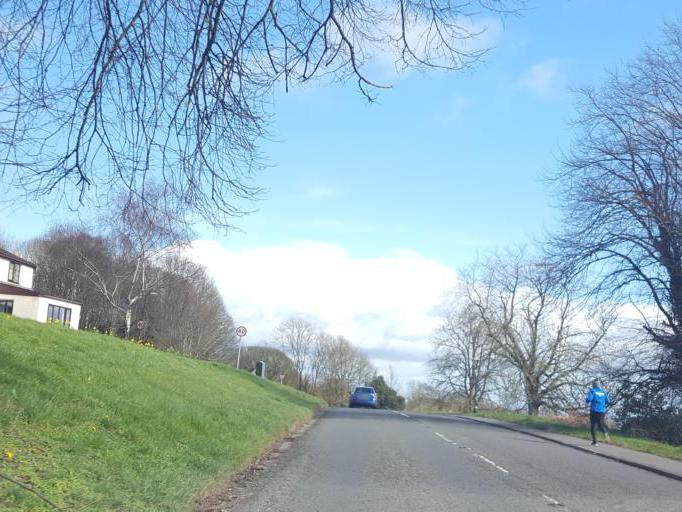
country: GB
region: England
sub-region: Worcestershire
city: Great Malvern
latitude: 52.0963
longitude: -2.3322
